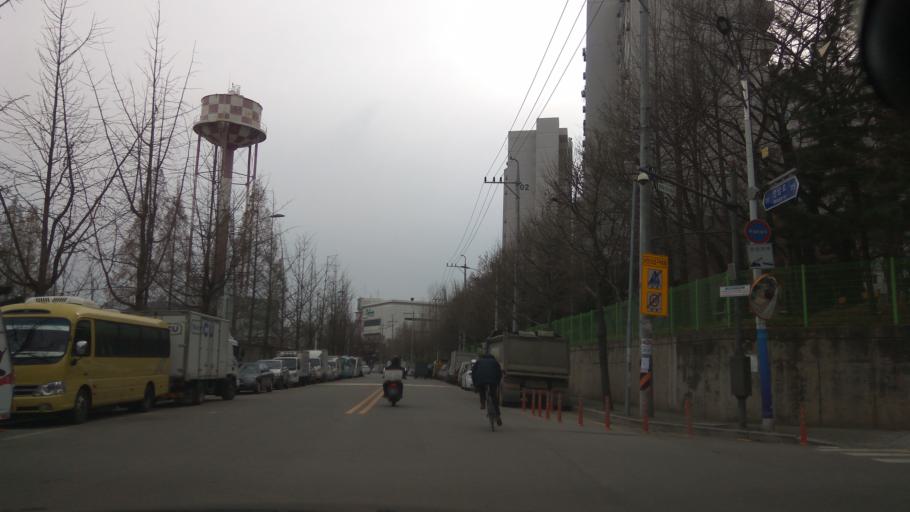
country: KR
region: Incheon
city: Incheon
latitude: 37.4932
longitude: 126.7100
